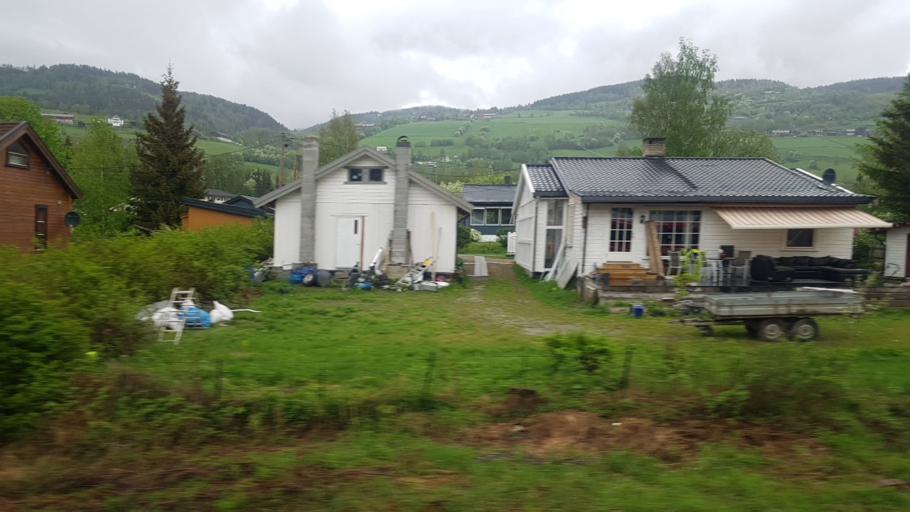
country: NO
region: Oppland
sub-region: Nord-Fron
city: Vinstra
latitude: 61.5851
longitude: 9.7547
